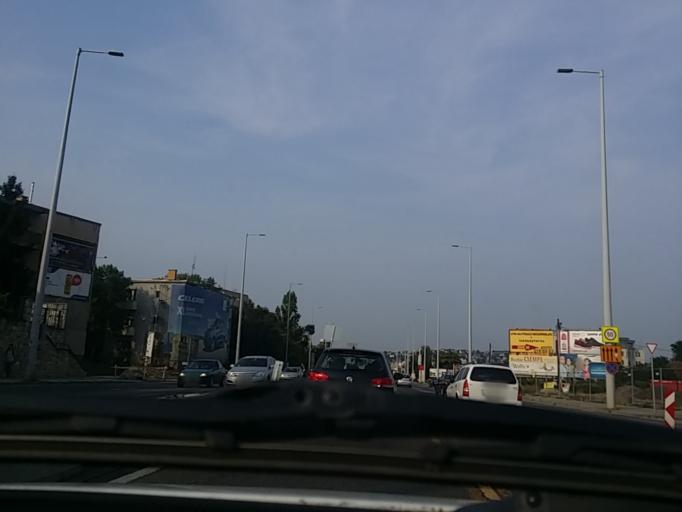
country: HU
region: Budapest
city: Budapest XI. keruelet
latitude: 47.4680
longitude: 19.0177
